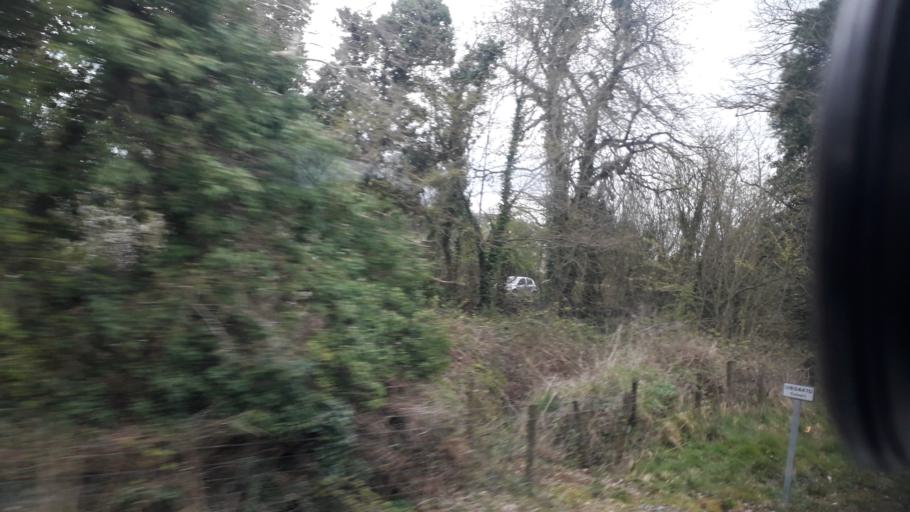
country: IE
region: Leinster
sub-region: An Longfort
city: Longford
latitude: 53.7234
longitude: -7.7673
